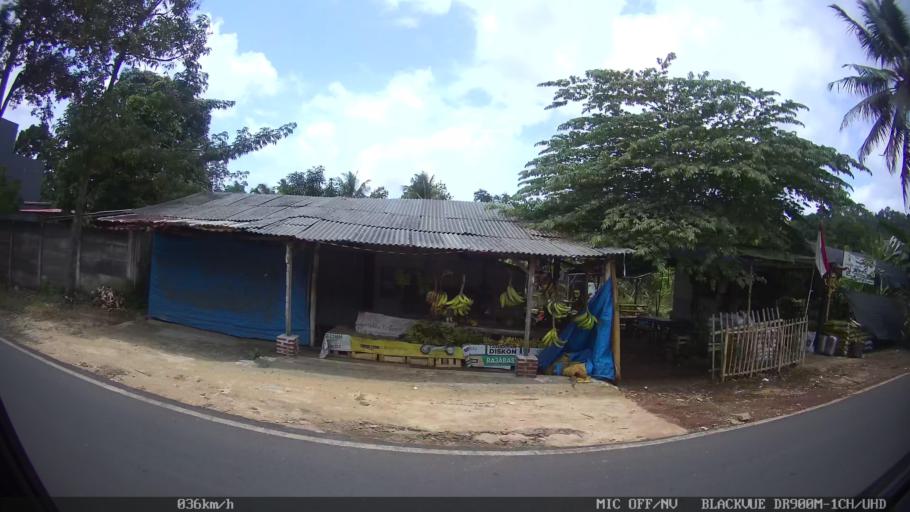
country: ID
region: Lampung
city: Bandarlampung
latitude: -5.4180
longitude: 105.2335
